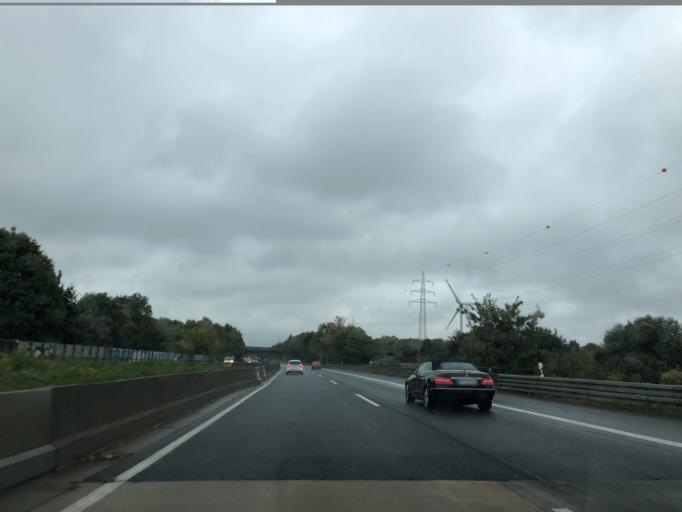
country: DE
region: North Rhine-Westphalia
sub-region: Regierungsbezirk Koln
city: Bedburg
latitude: 50.9706
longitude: 6.5630
